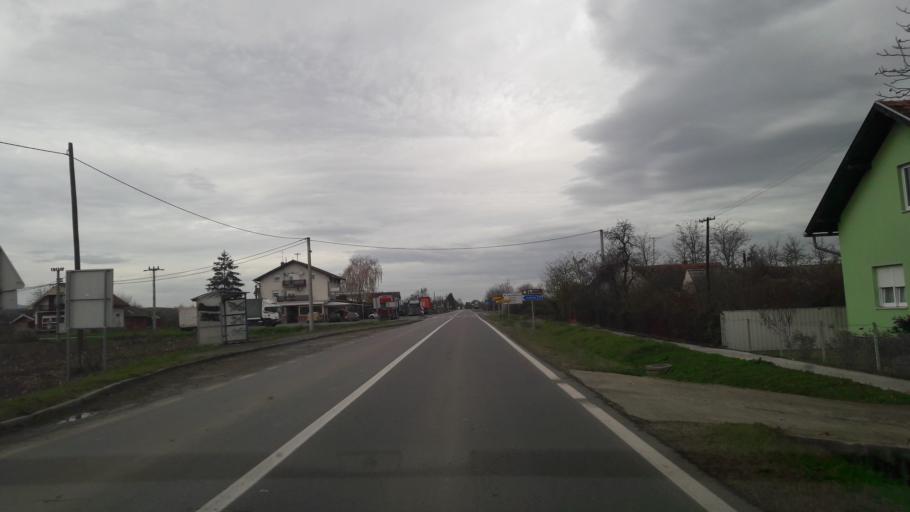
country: HR
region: Osjecko-Baranjska
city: Fericanci
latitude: 45.5318
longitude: 17.9472
